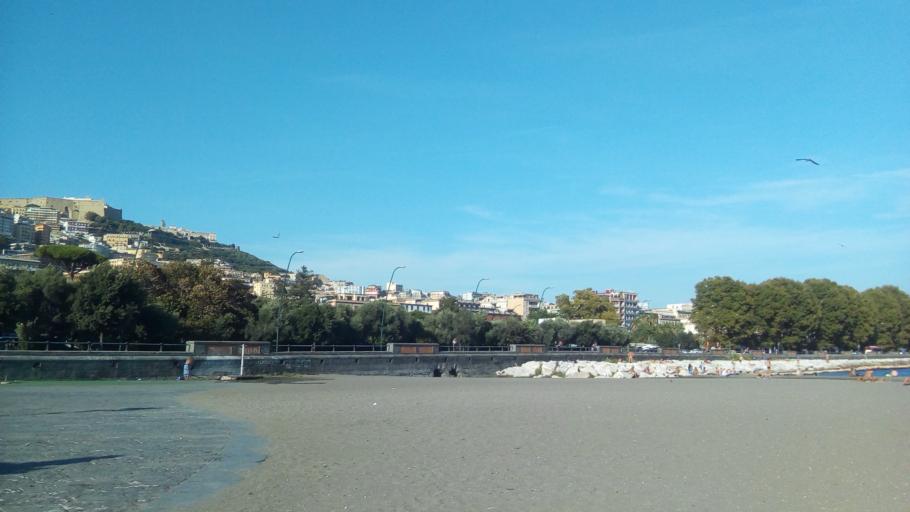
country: IT
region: Campania
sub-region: Provincia di Napoli
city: Napoli
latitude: 40.8314
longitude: 14.2300
